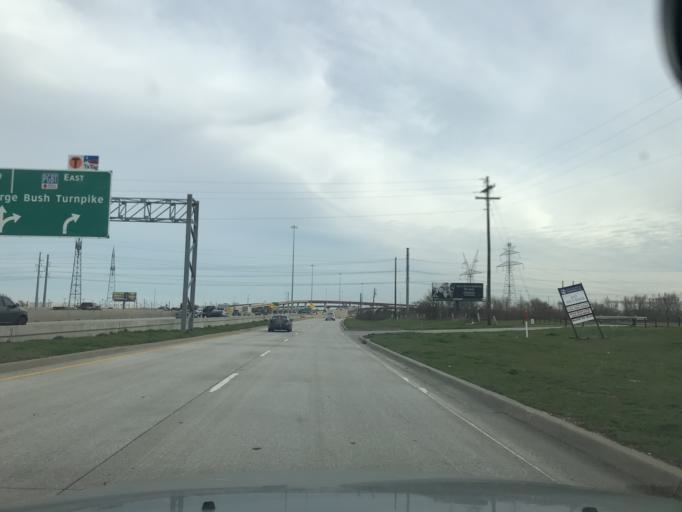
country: US
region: Texas
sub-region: Dallas County
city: Carrollton
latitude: 32.9886
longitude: -96.9401
